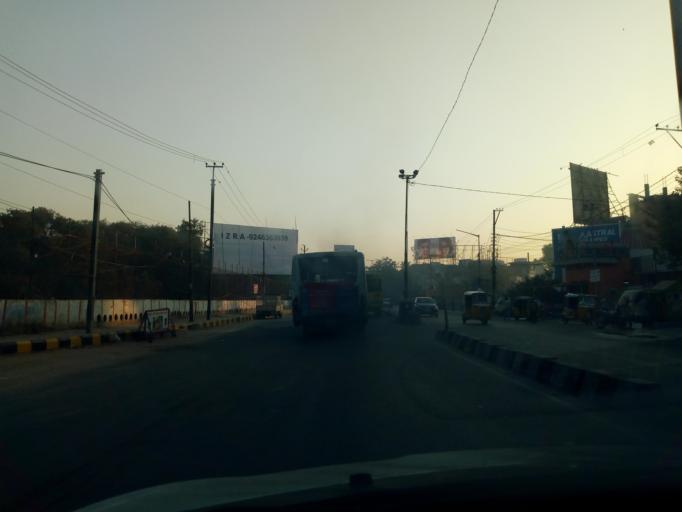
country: IN
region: Telangana
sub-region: Rangareddi
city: Gaddi Annaram
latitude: 17.3949
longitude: 78.5010
